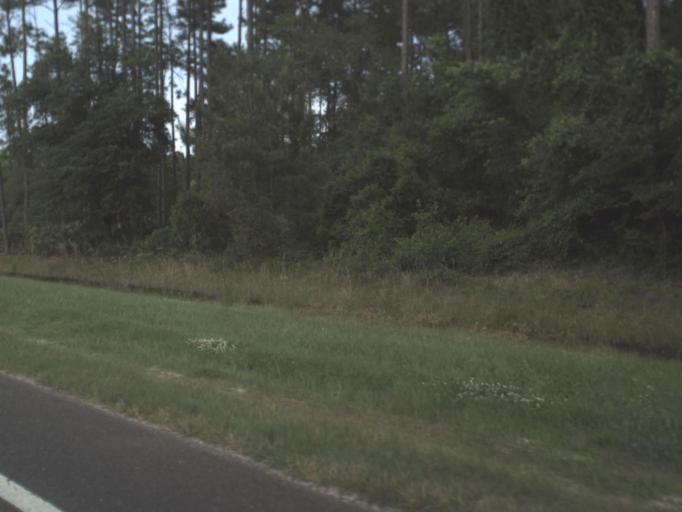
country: US
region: Florida
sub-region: Putnam County
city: East Palatka
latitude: 29.7322
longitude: -81.4773
